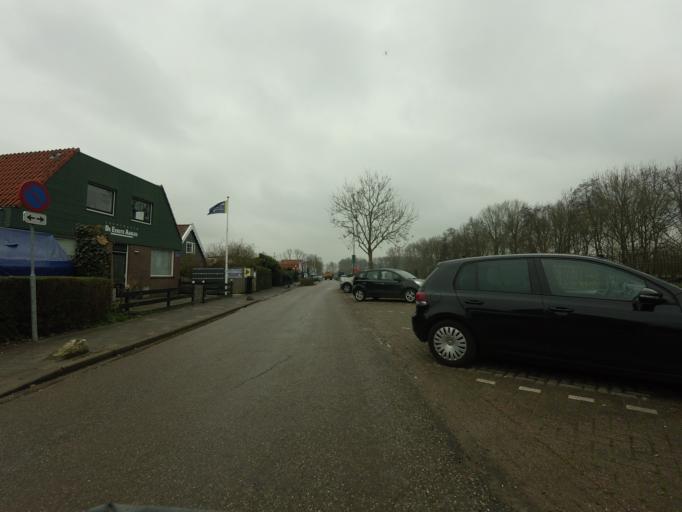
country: NL
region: Utrecht
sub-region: Stichtse Vecht
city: Breukelen
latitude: 52.1776
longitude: 5.0208
